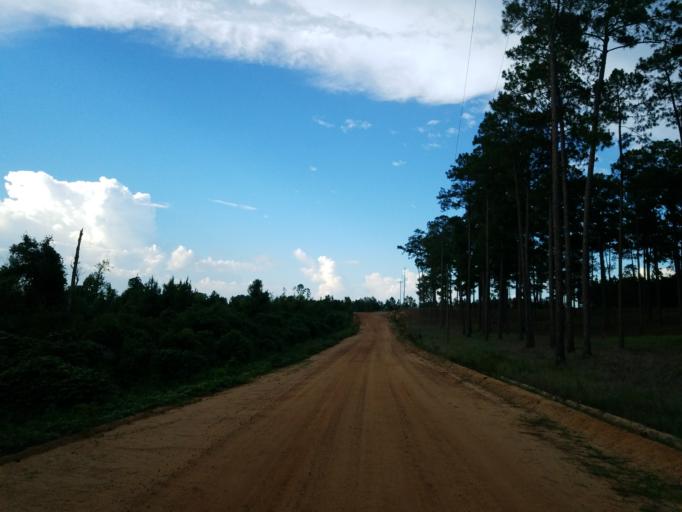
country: US
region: Georgia
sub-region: Tift County
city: Omega
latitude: 31.2711
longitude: -83.5288
